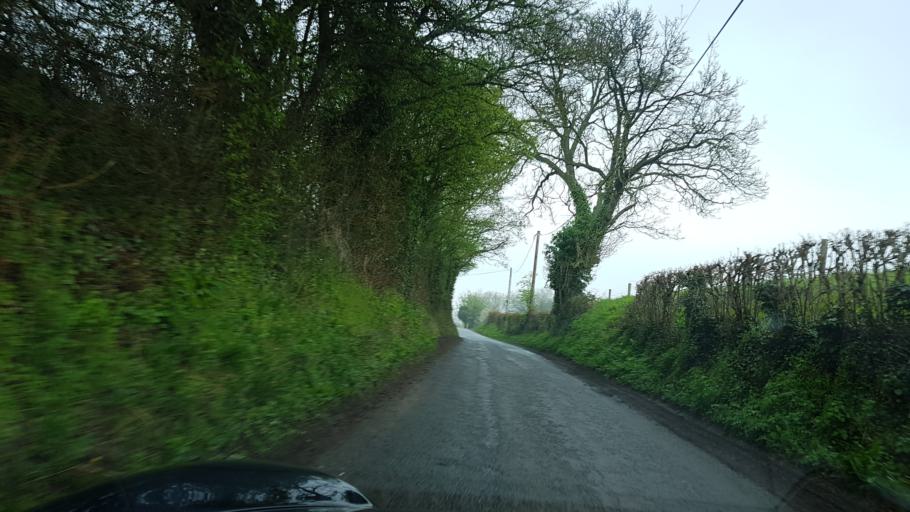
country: GB
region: England
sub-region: Herefordshire
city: Yatton
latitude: 52.0024
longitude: -2.5189
